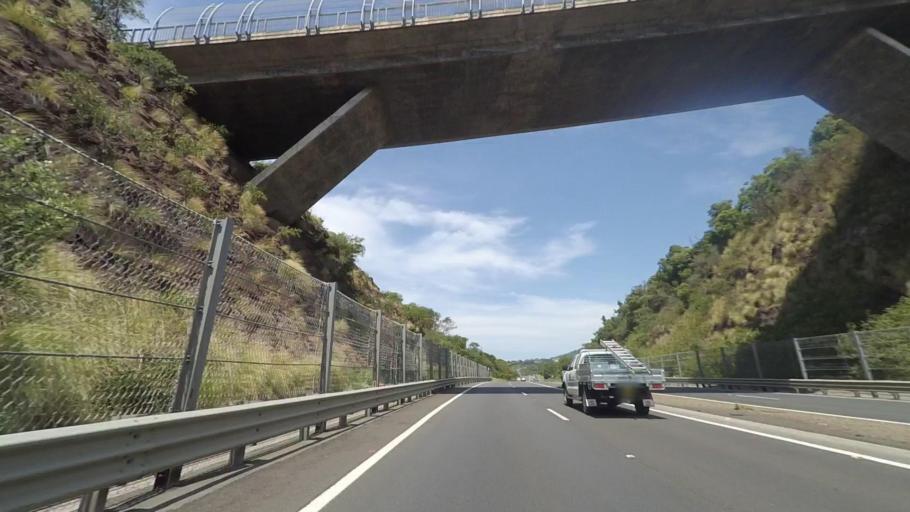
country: AU
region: New South Wales
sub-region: Kiama
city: Kiama
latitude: -34.6815
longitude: 150.8444
